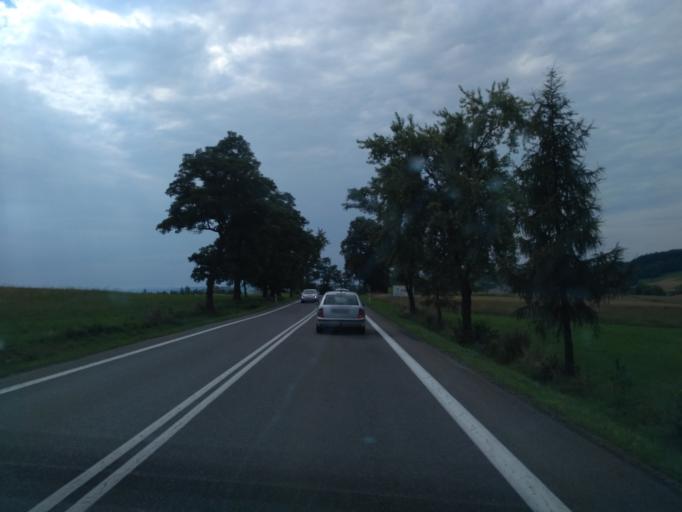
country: PL
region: Subcarpathian Voivodeship
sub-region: Powiat sanocki
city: Strachocina
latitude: 49.6323
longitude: 22.0958
